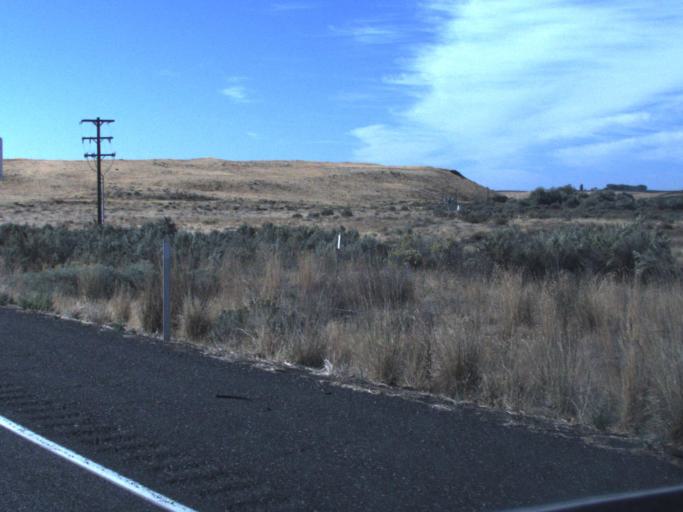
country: US
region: Washington
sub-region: Franklin County
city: Pasco
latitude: 46.4312
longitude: -119.0251
